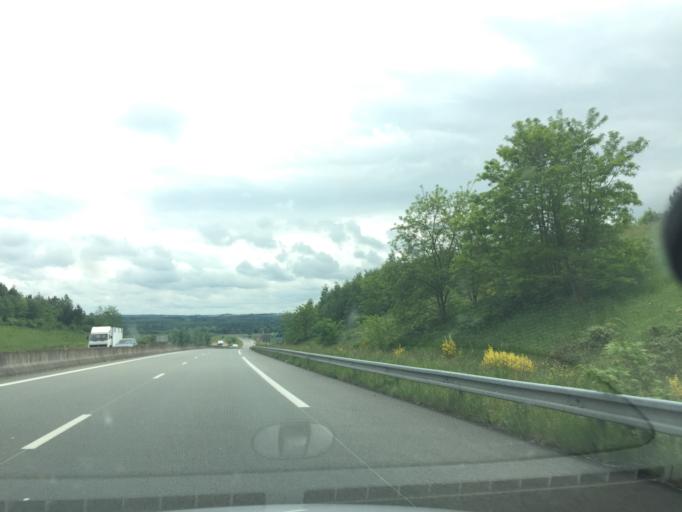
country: FR
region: Pays de la Loire
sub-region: Departement de la Sarthe
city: Luceau
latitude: 47.6799
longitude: 0.3702
